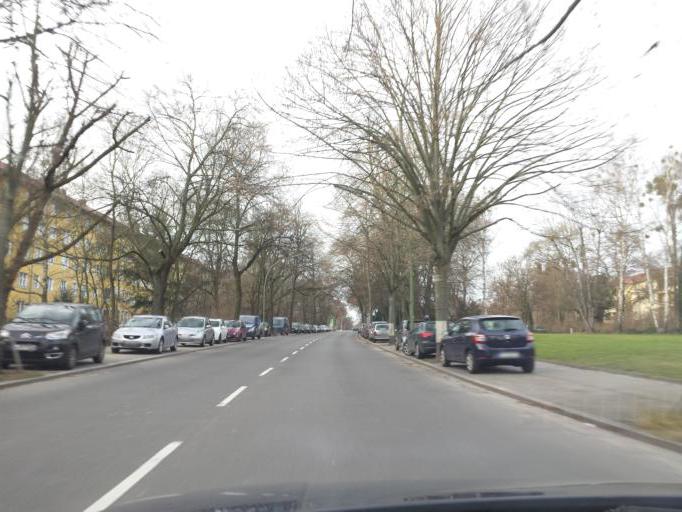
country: DE
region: Berlin
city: Zehlendorf Bezirk
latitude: 52.4342
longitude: 13.2754
